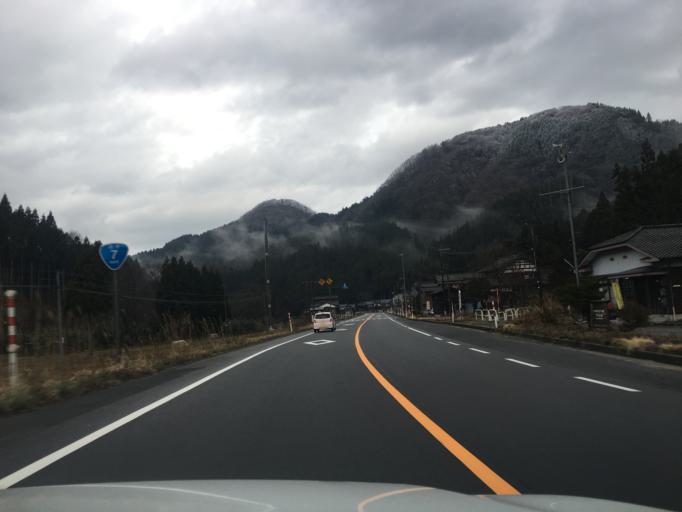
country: JP
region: Niigata
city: Murakami
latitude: 38.4713
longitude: 139.5537
